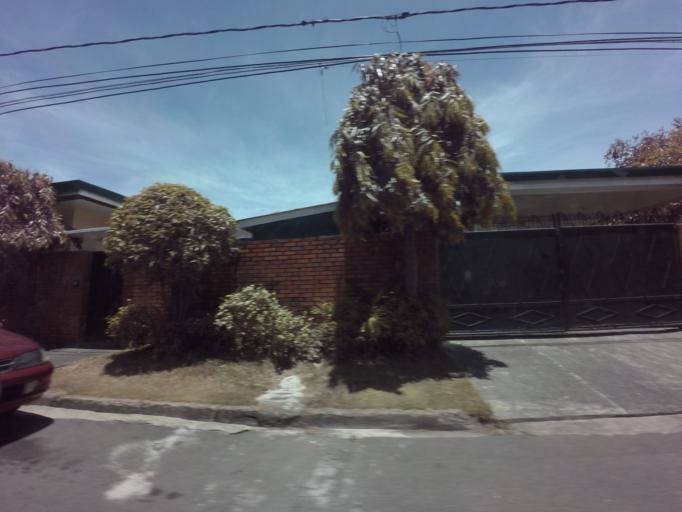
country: PH
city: Sambayanihan People's Village
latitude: 14.4869
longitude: 121.0379
